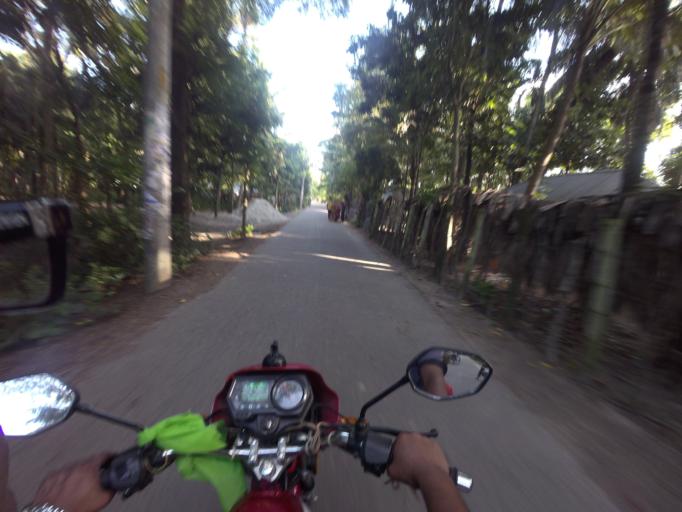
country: BD
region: Khulna
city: Khulna
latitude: 22.9146
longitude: 89.5196
